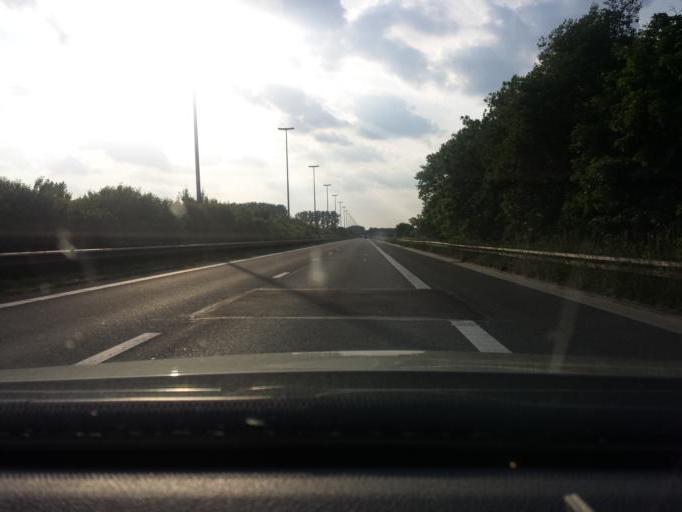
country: BE
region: Flanders
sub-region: Provincie Limburg
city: Hoeselt
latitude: 50.8805
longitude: 5.4623
